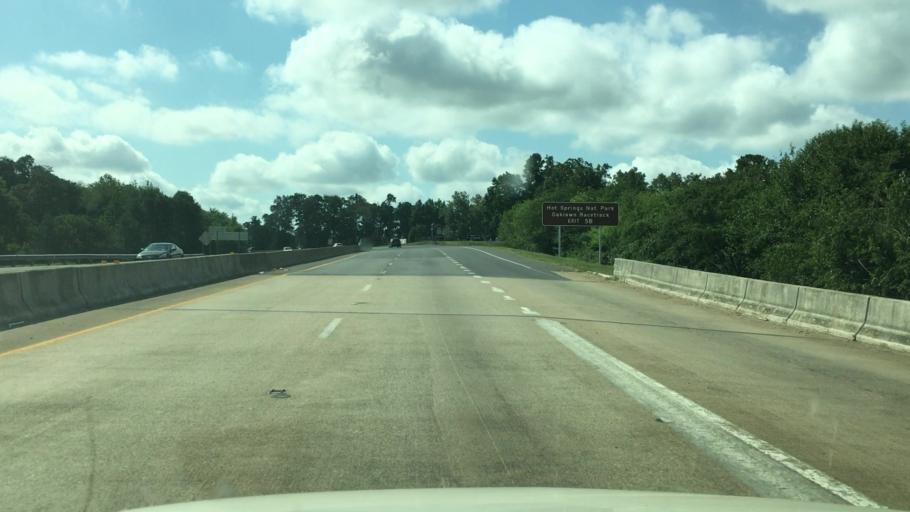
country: US
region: Arkansas
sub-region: Garland County
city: Lake Hamilton
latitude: 34.4682
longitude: -93.0881
